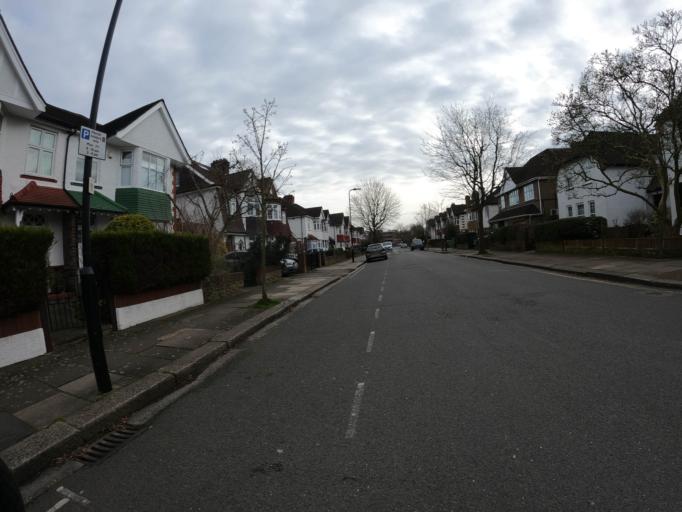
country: GB
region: England
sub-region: Greater London
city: Acton
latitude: 51.5072
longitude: -0.2883
